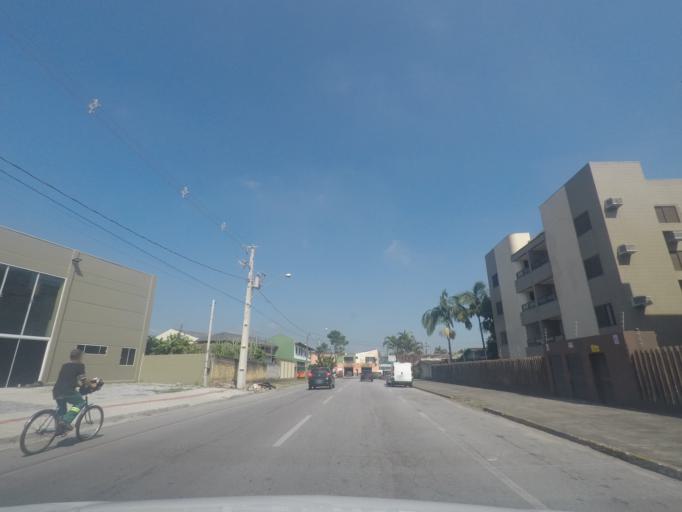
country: BR
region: Parana
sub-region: Paranagua
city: Paranagua
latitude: -25.5302
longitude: -48.5218
